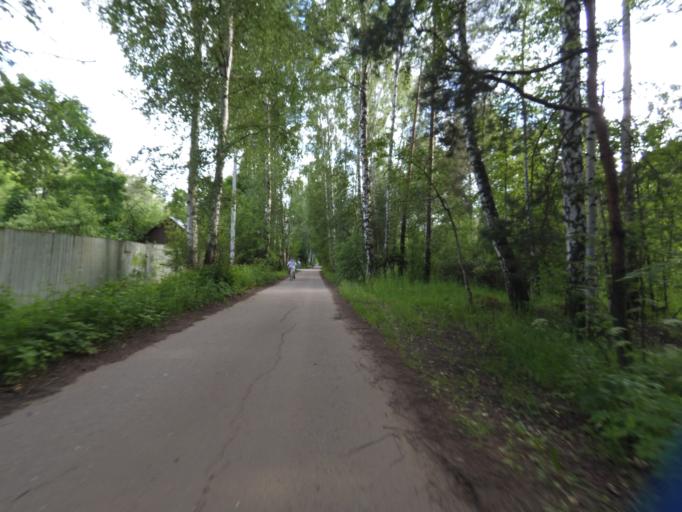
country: RU
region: Moskovskaya
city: Nekrasovskiy
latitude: 56.0763
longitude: 37.4975
